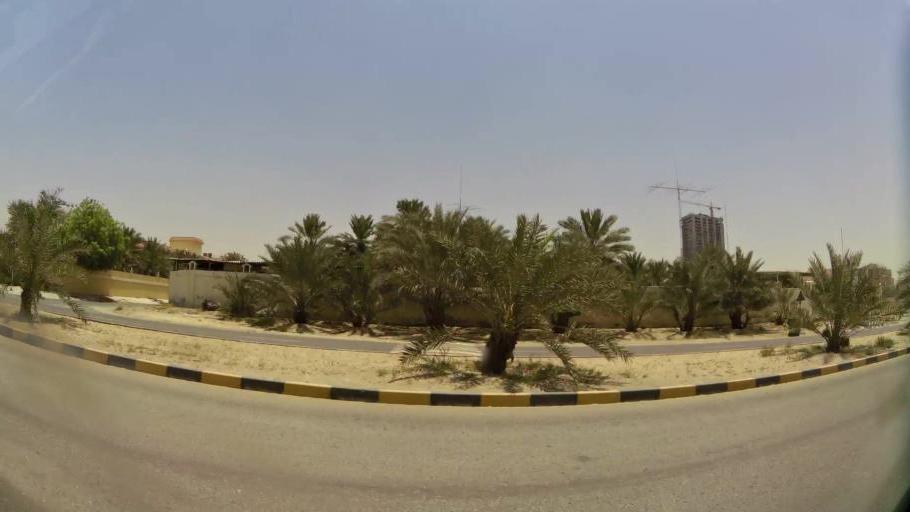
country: AE
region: Ajman
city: Ajman
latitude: 25.4007
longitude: 55.5082
